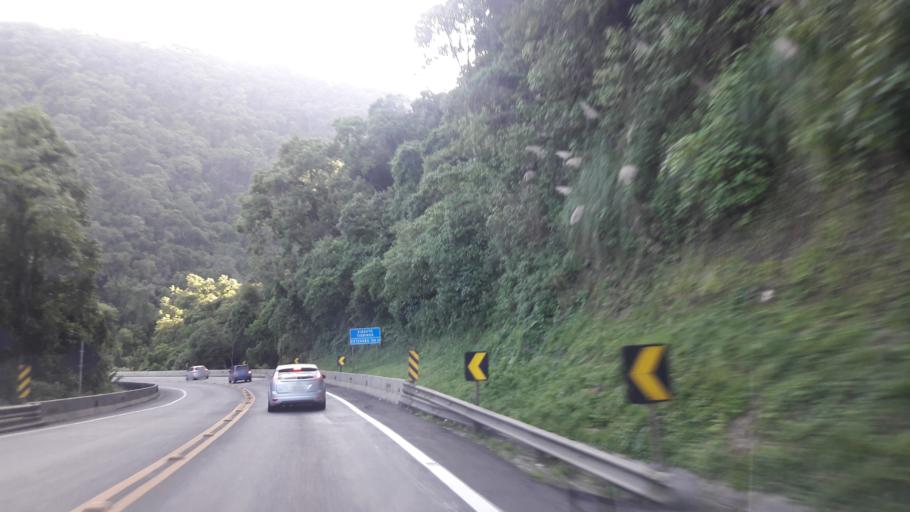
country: BR
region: Parana
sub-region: Prudentopolis
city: Prudentopolis
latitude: -25.3213
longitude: -51.1961
